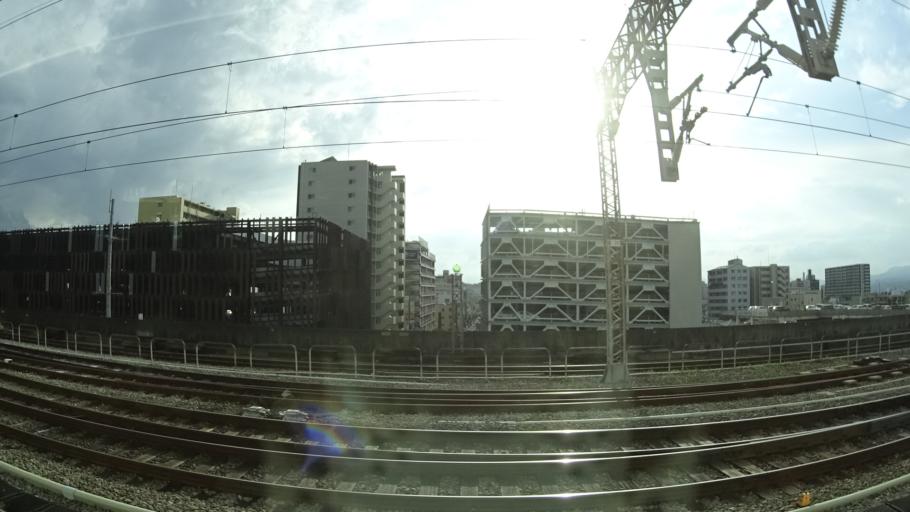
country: JP
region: Gunma
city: Takasaki
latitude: 36.3266
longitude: 139.0125
